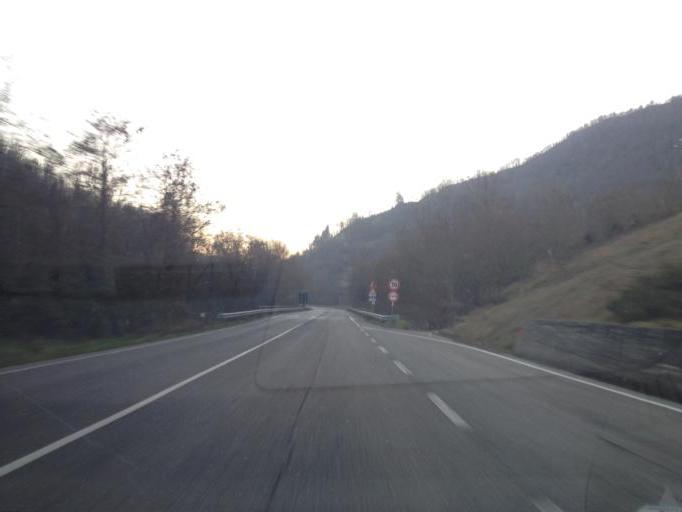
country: IT
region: The Marches
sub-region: Provincia di Ascoli Piceno
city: Arquata del Tronto
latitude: 42.7655
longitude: 13.2880
